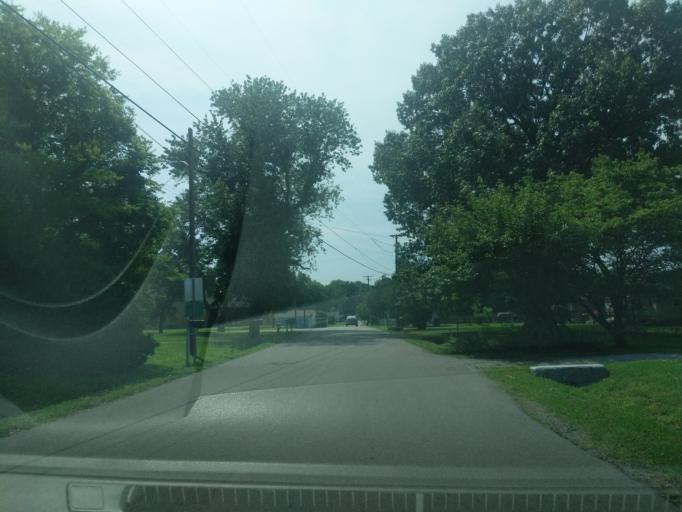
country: US
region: Tennessee
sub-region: Davidson County
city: Lakewood
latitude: 36.2722
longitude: -86.6690
